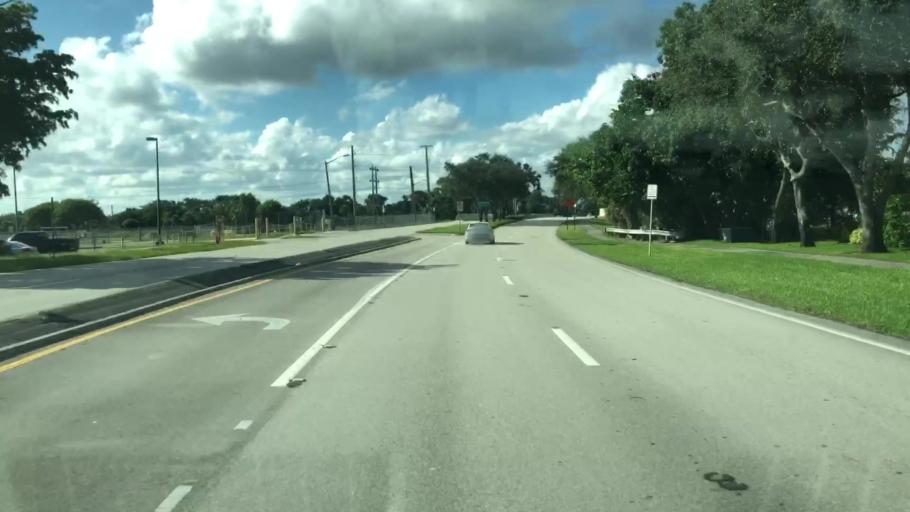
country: US
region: Florida
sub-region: Broward County
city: Tamarac
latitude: 26.2316
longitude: -80.2700
